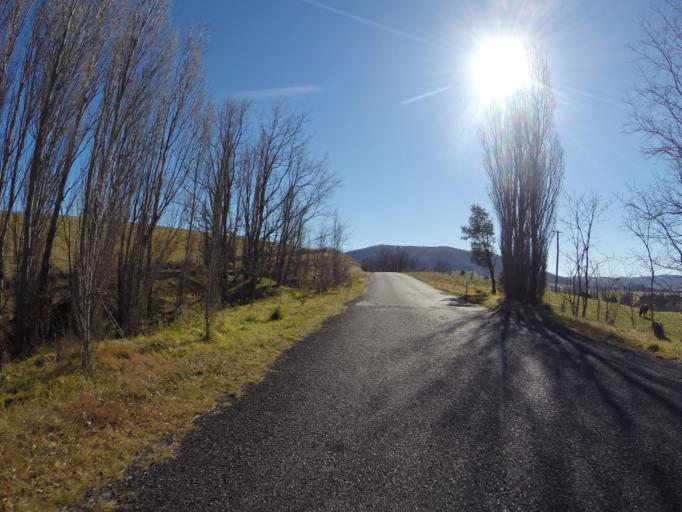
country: AU
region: New South Wales
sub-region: Oberon
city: Oberon
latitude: -33.5495
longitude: 149.8728
